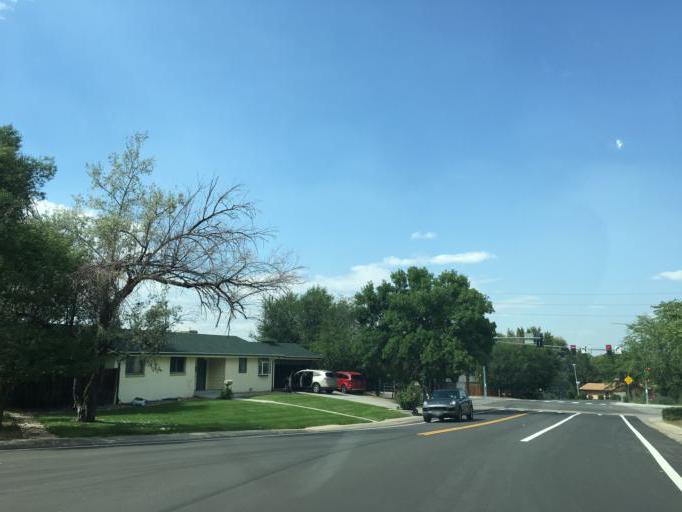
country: US
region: Colorado
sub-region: Jefferson County
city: Applewood
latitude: 39.7613
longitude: -105.1300
